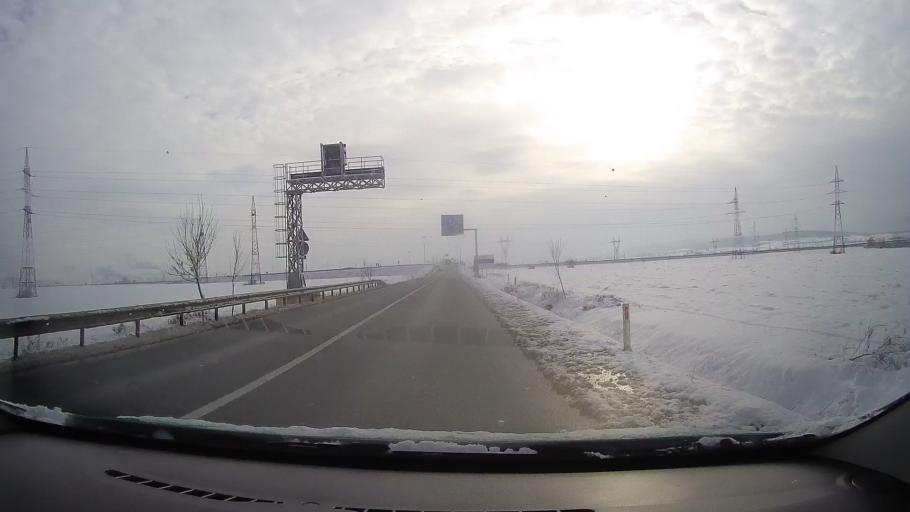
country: RO
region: Alba
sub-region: Municipiul Sebes
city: Lancram
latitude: 45.9816
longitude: 23.5180
